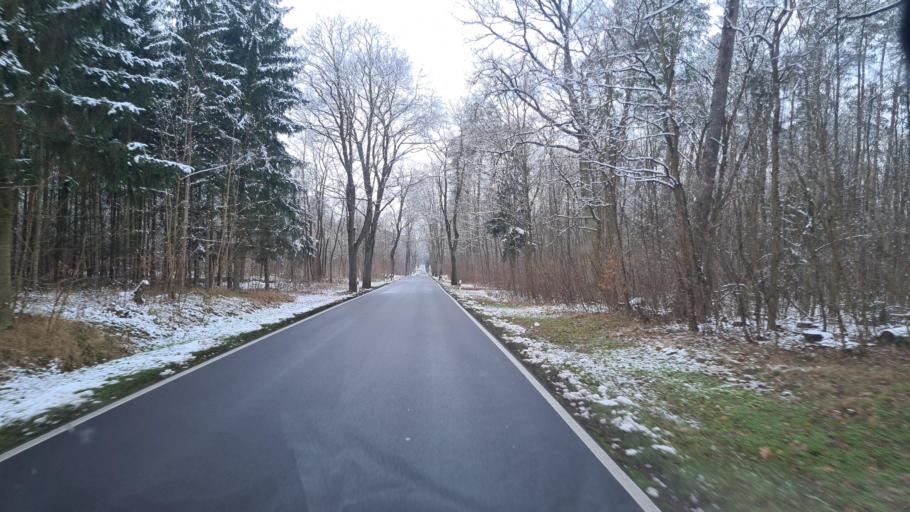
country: DE
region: Brandenburg
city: Strausberg
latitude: 52.5540
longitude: 13.9141
